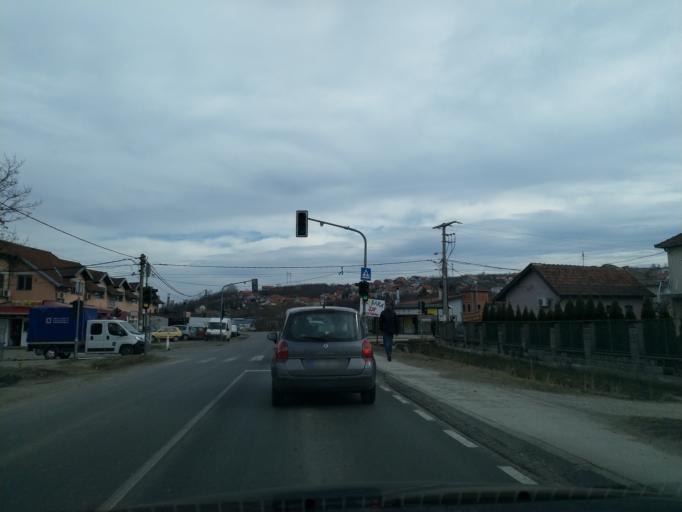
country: RS
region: Central Serbia
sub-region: Belgrade
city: Zvezdara
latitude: 44.7277
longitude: 20.5755
